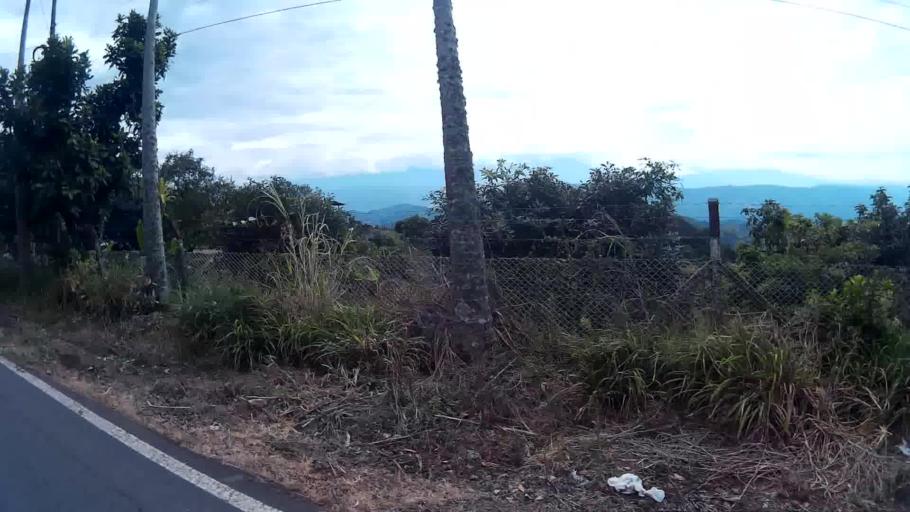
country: CO
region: Risaralda
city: Marsella
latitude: 4.8870
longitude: -75.7512
